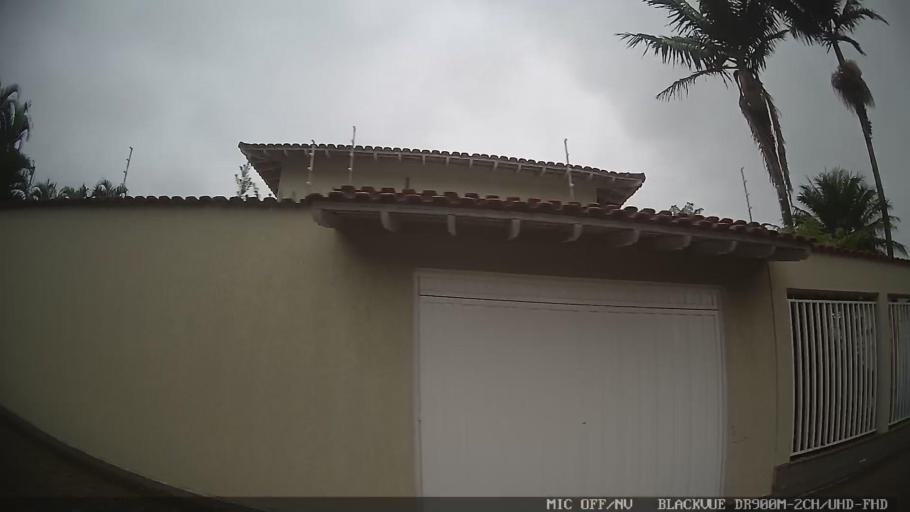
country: BR
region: Sao Paulo
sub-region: Mogi das Cruzes
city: Mogi das Cruzes
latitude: -23.5247
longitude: -46.1671
